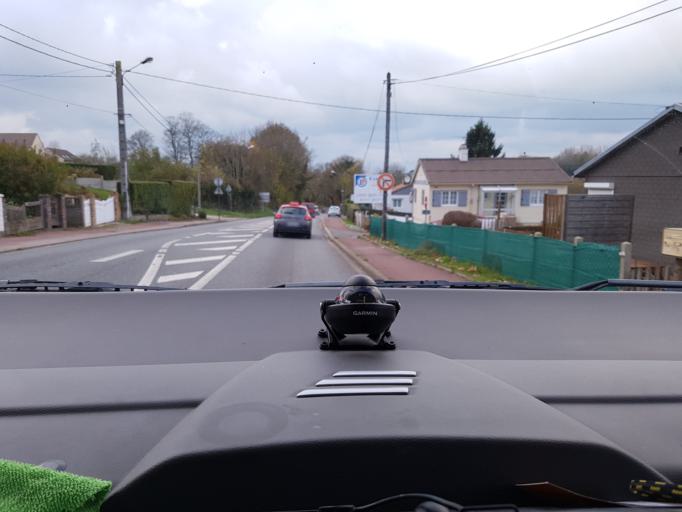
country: FR
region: Haute-Normandie
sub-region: Departement de la Seine-Maritime
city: Rouxmesnil-Bouteilles
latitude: 49.9091
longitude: 1.0584
